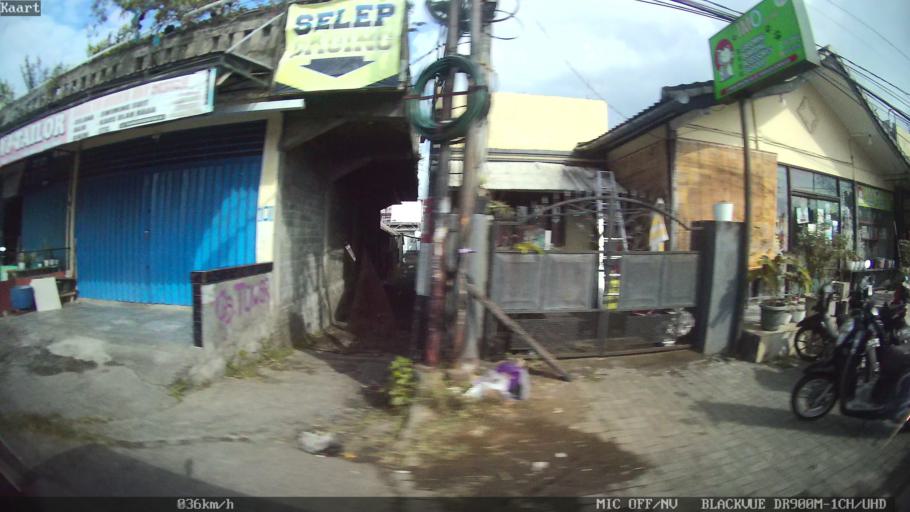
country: ID
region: Bali
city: Karyadharma
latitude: -8.6956
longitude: 115.1955
